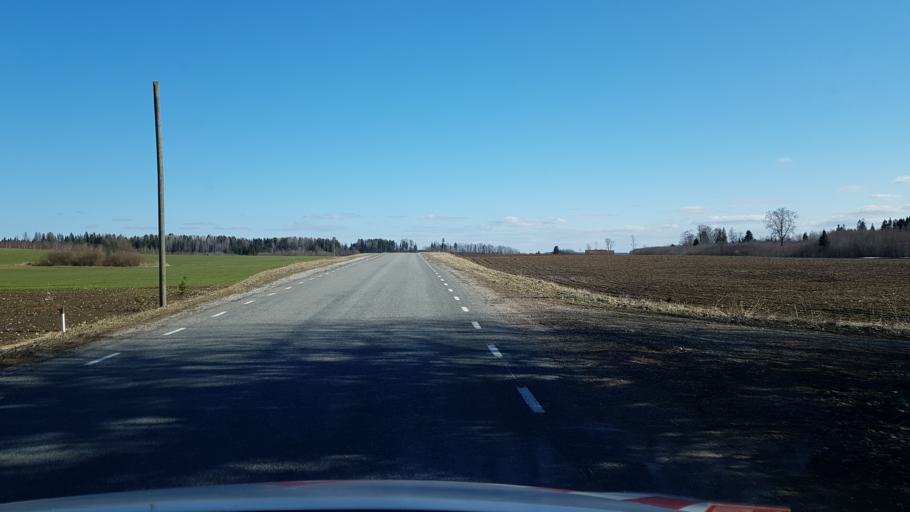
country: EE
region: Laeaene-Virumaa
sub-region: Kadrina vald
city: Kadrina
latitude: 59.3604
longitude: 26.0603
